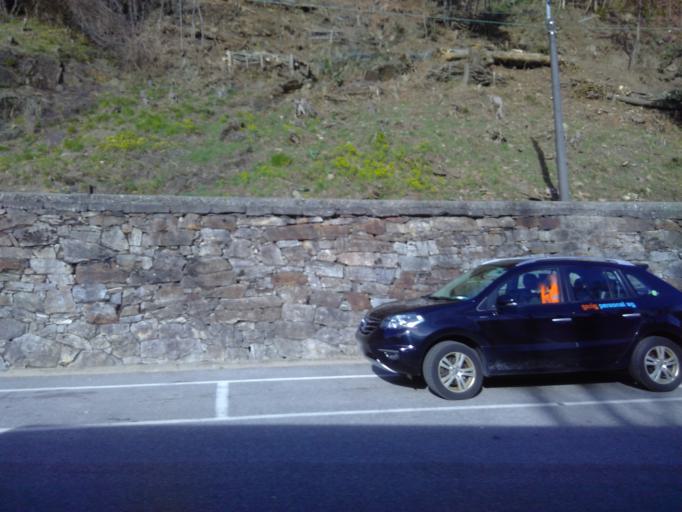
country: CH
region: Ticino
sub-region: Locarno District
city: Losone
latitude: 46.1792
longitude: 8.7613
